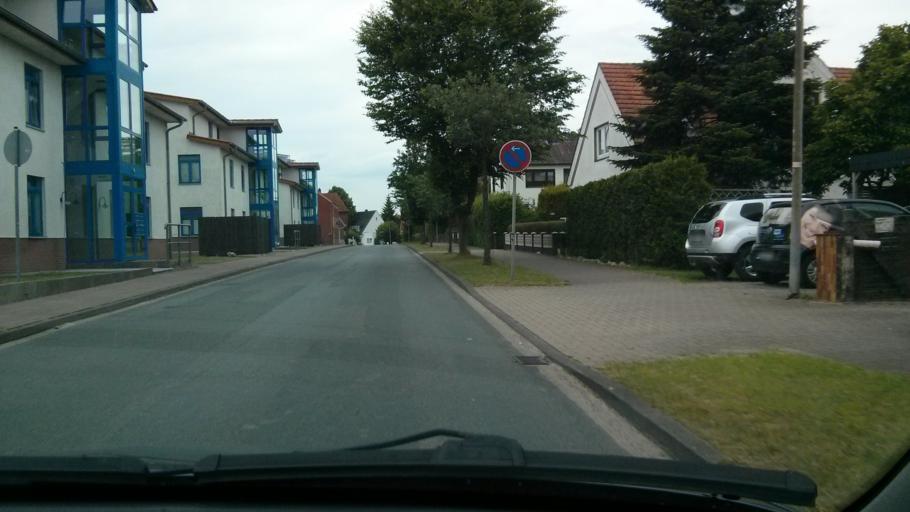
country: DE
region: Lower Saxony
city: Loxstedt
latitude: 53.4679
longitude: 8.6509
